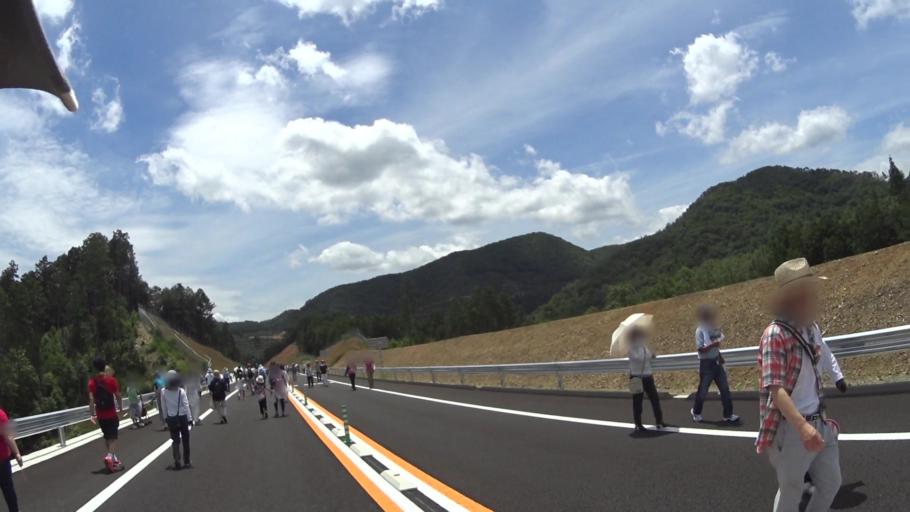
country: JP
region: Kyoto
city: Ayabe
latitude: 35.1648
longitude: 135.3859
